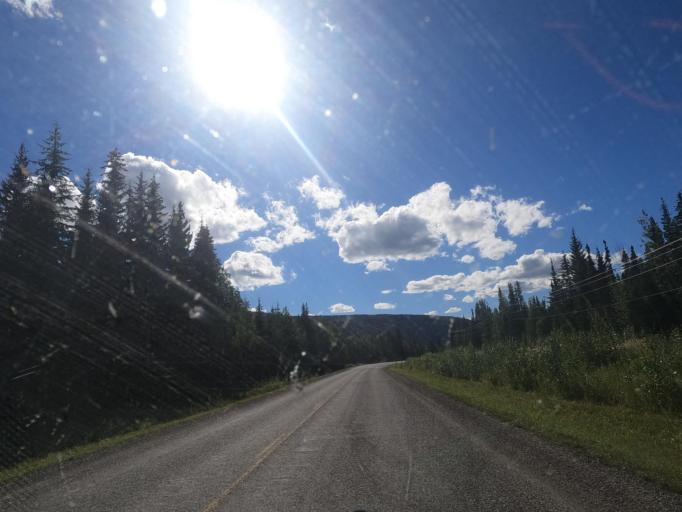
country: CA
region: Yukon
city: Dawson City
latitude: 64.0324
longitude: -139.1653
